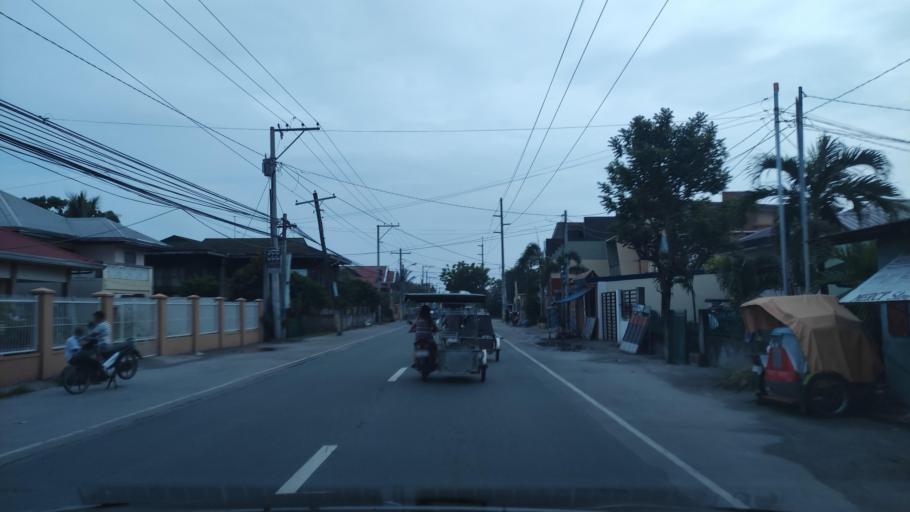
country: PH
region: Central Luzon
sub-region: Province of Pampanga
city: Santa Ana
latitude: 15.1080
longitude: 120.7716
